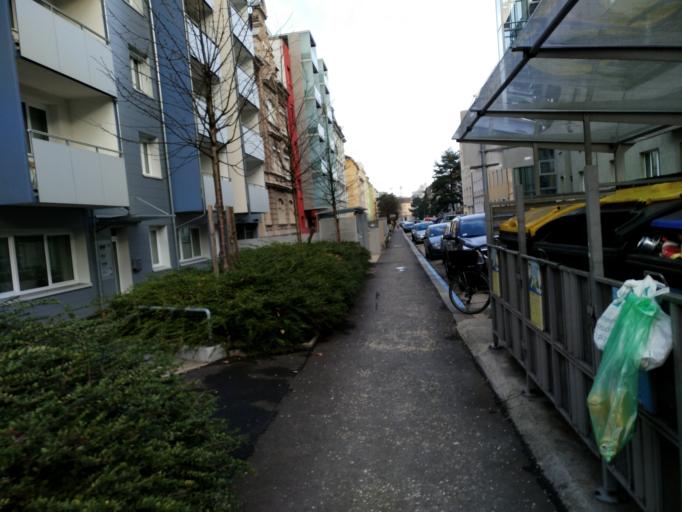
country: AT
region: Upper Austria
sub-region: Linz Stadt
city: Linz
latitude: 48.2919
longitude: 14.2866
